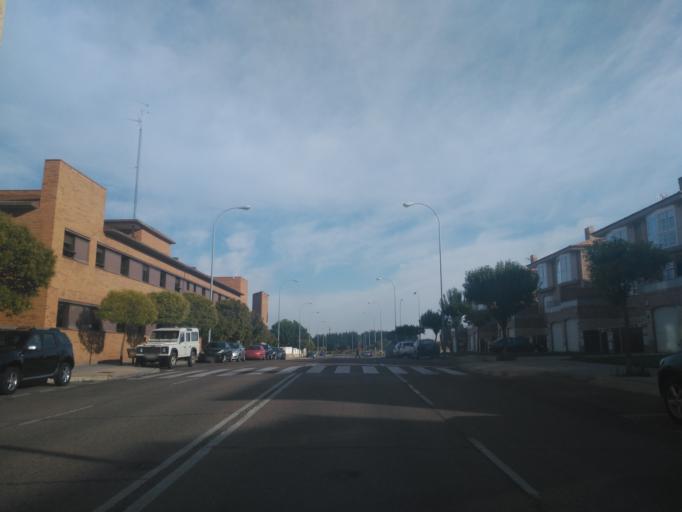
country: ES
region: Castille and Leon
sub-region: Provincia de Salamanca
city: Salamanca
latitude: 40.9823
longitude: -5.6662
